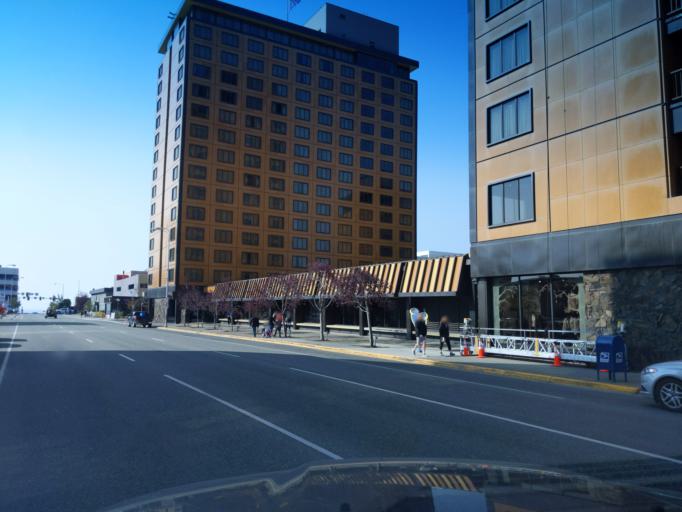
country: US
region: Alaska
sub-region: Anchorage Municipality
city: Anchorage
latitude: 61.2175
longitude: -149.8997
